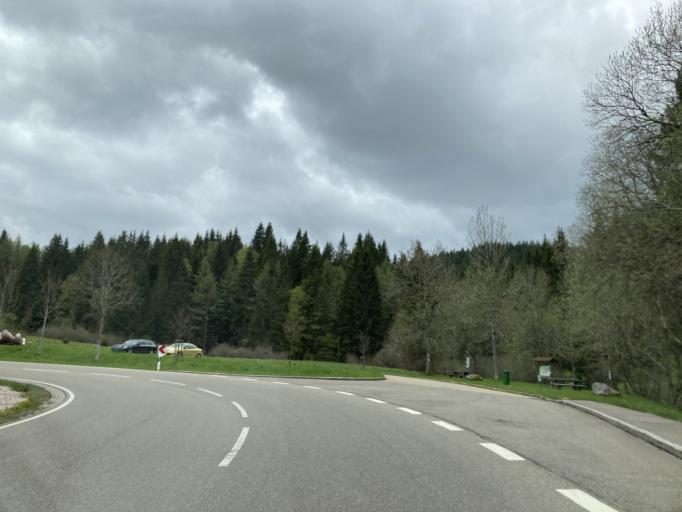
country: DE
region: Baden-Wuerttemberg
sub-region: Freiburg Region
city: Schonach im Schwarzwald
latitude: 48.1291
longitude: 8.1565
